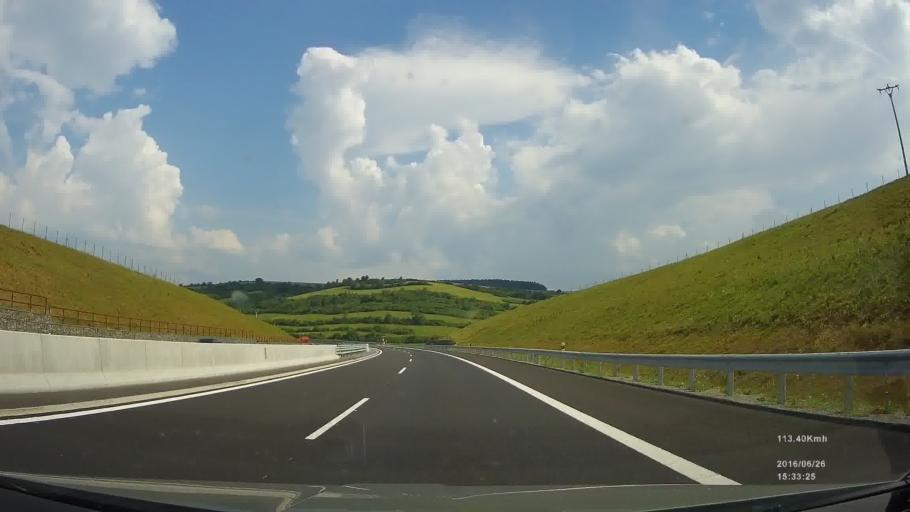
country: SK
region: Presovsky
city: Sabinov
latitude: 49.0018
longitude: 21.0573
